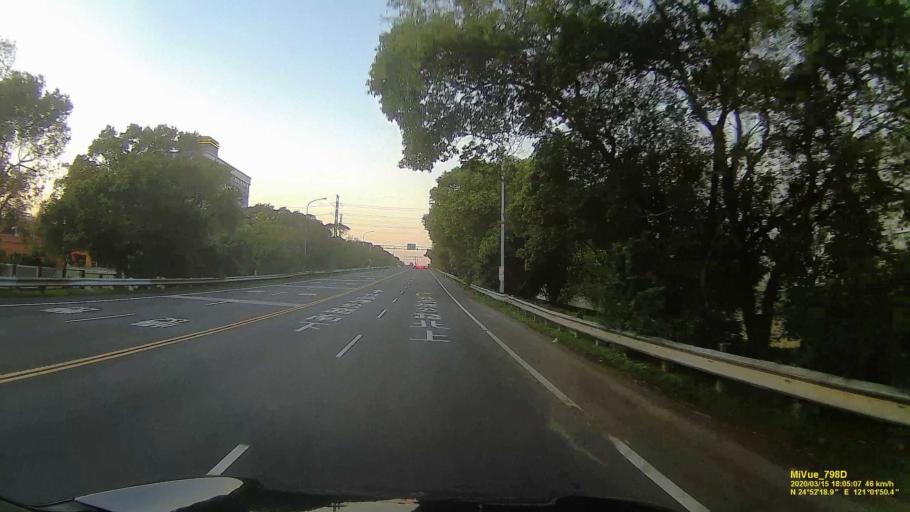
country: TW
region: Taiwan
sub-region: Hsinchu
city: Zhubei
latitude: 24.8721
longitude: 121.0306
